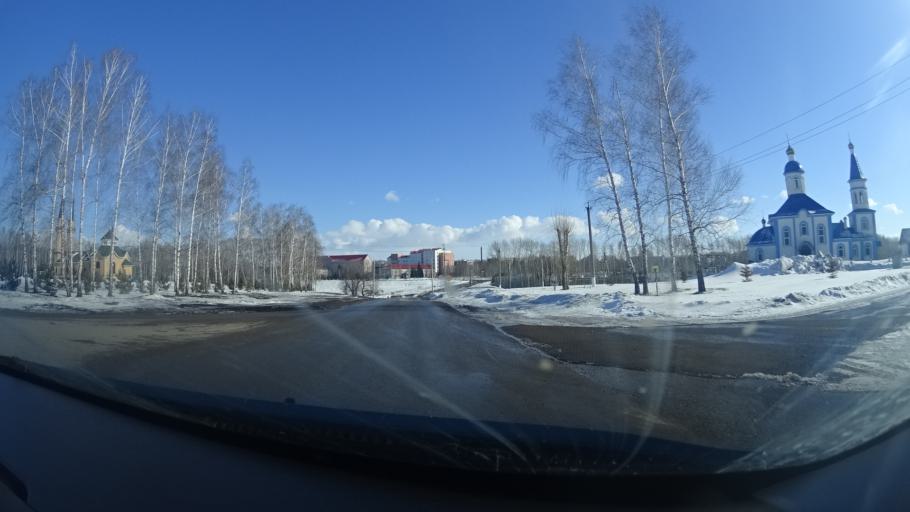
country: RU
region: Bashkortostan
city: Chishmy
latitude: 54.5927
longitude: 55.3649
